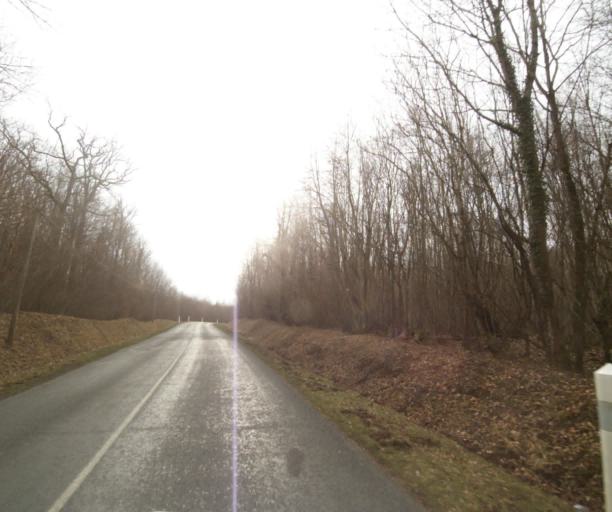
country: FR
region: Champagne-Ardenne
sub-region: Departement de la Haute-Marne
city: Villiers-en-Lieu
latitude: 48.6947
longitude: 4.8925
